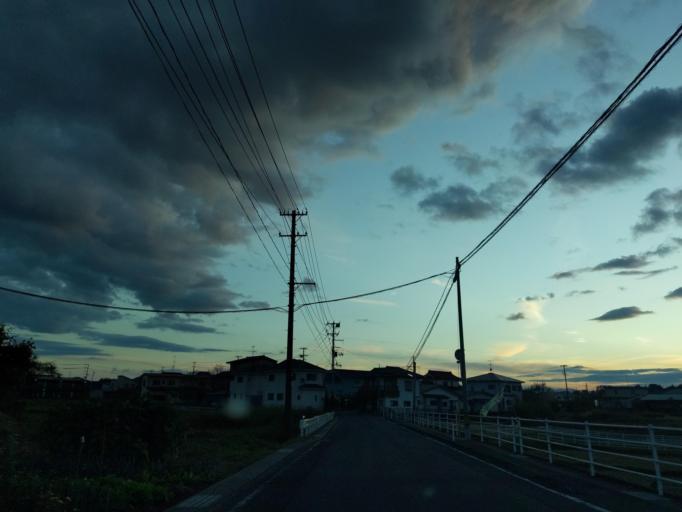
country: JP
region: Fukushima
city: Motomiya
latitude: 37.5111
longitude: 140.4049
